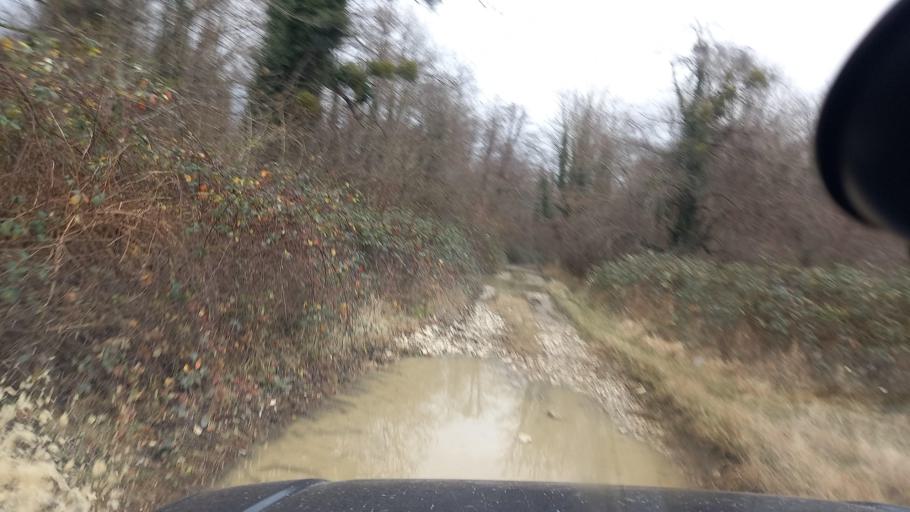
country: RU
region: Krasnodarskiy
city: Pshada
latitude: 44.4888
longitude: 38.4144
